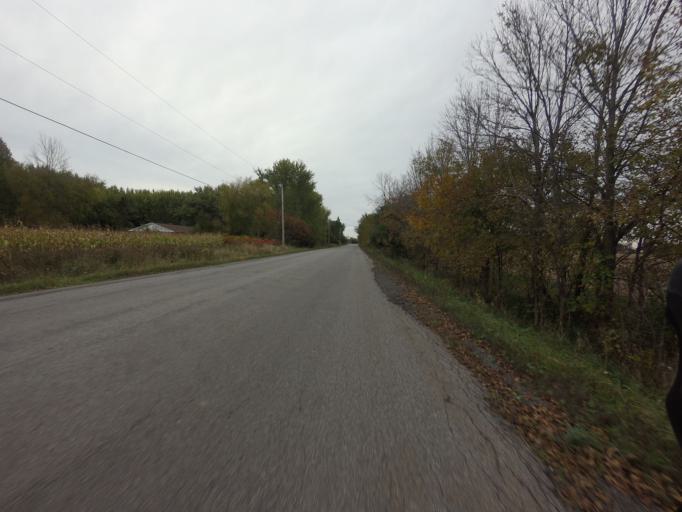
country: CA
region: Ontario
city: Bells Corners
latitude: 45.1079
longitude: -75.7310
